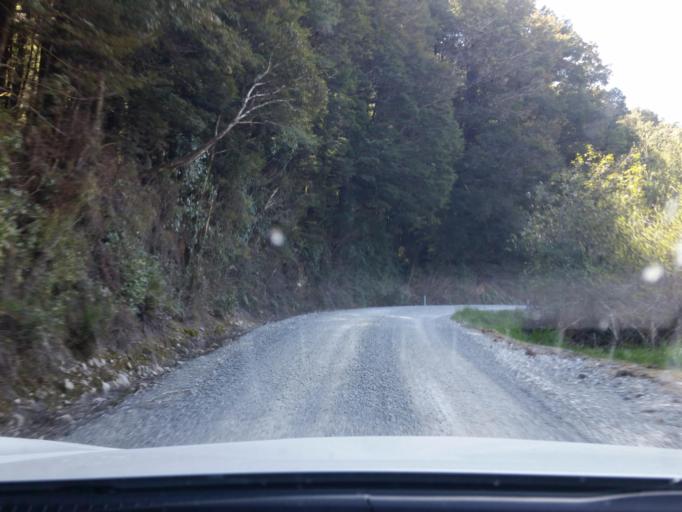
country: NZ
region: West Coast
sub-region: Buller District
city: Westport
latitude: -41.8745
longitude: 172.2469
